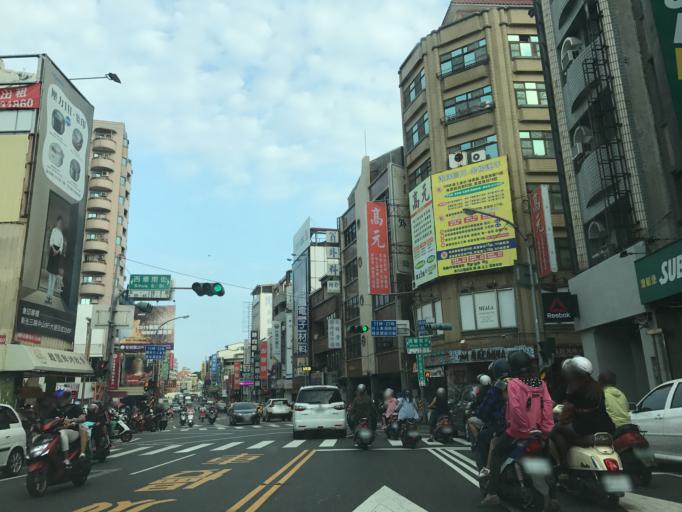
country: TW
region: Taiwan
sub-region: Tainan
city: Tainan
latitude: 22.9945
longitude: 120.2092
